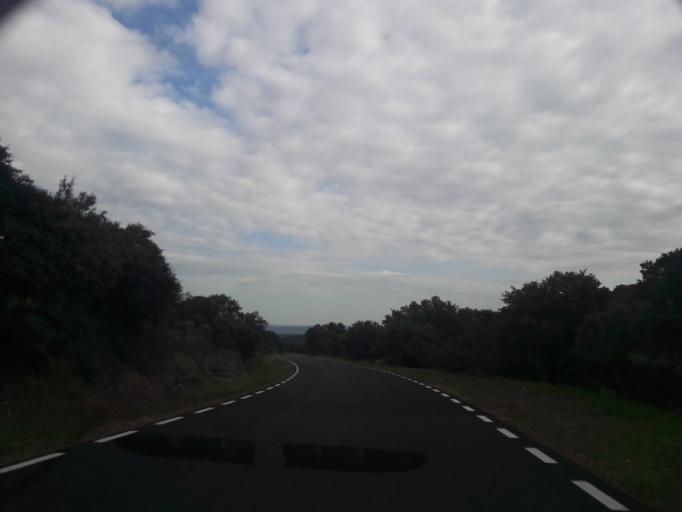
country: ES
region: Castille and Leon
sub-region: Provincia de Salamanca
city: Pastores
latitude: 40.5193
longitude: -6.5267
